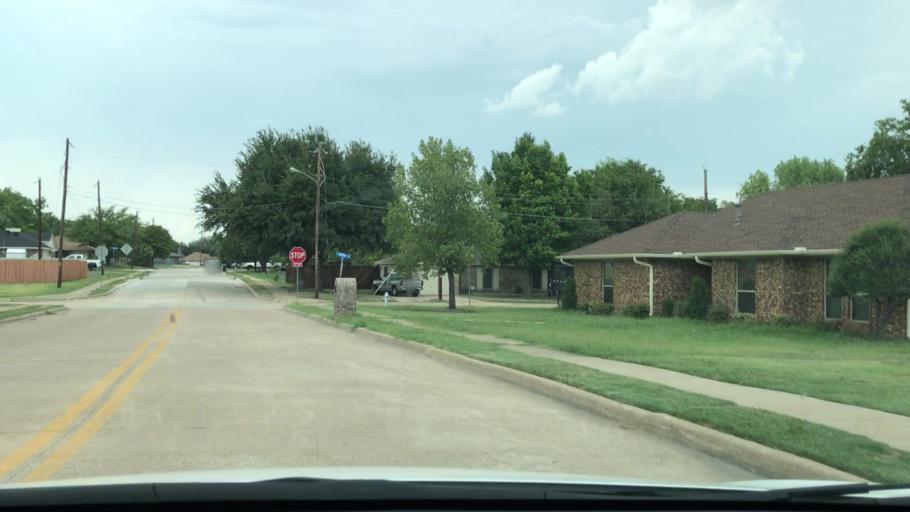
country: US
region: Texas
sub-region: Dallas County
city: Sachse
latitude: 32.9769
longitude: -96.5833
